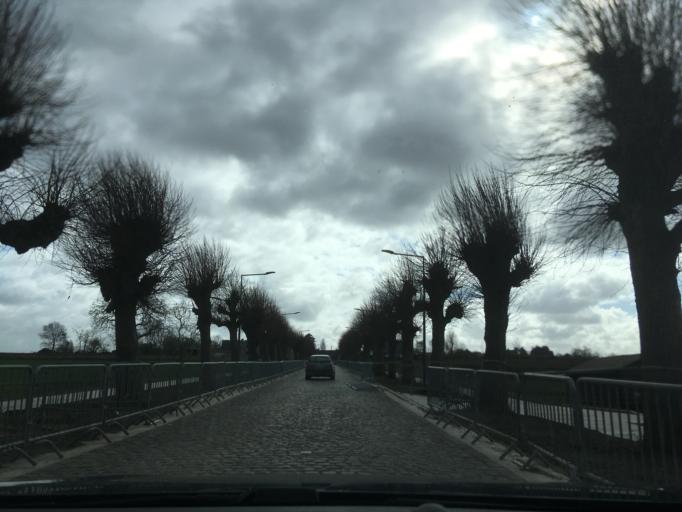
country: BE
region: Flanders
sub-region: Provincie West-Vlaanderen
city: Hooglede
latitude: 50.9913
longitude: 3.1039
